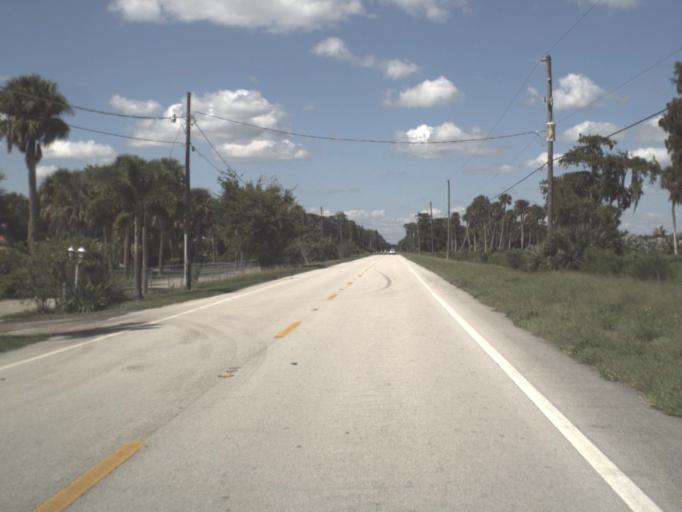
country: US
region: Florida
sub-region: Okeechobee County
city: Taylor Creek
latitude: 27.1673
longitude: -80.7194
